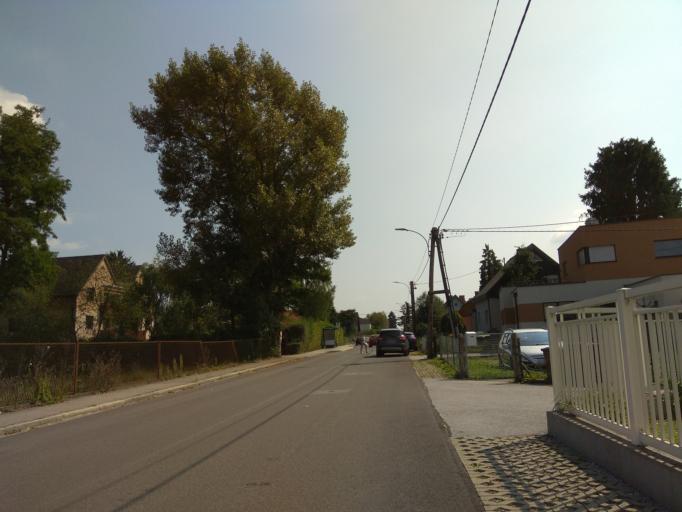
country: AT
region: Styria
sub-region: Politischer Bezirk Graz-Umgebung
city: Feldkirchen bei Graz
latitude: 47.0287
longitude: 15.4545
